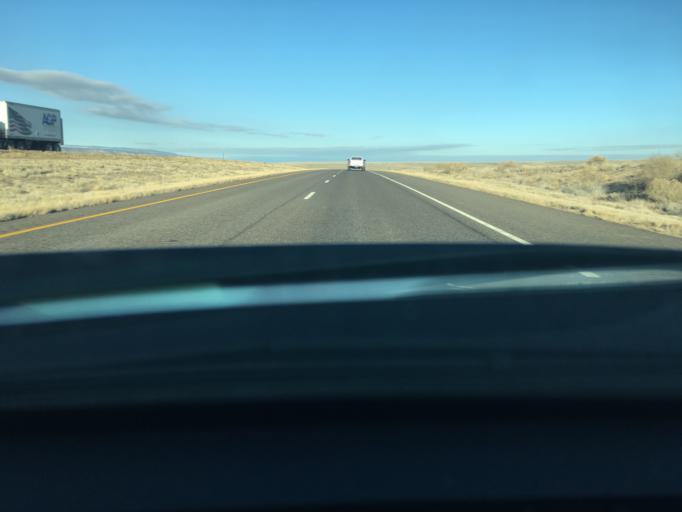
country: US
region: Colorado
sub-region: Delta County
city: Delta
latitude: 38.8002
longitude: -108.2683
